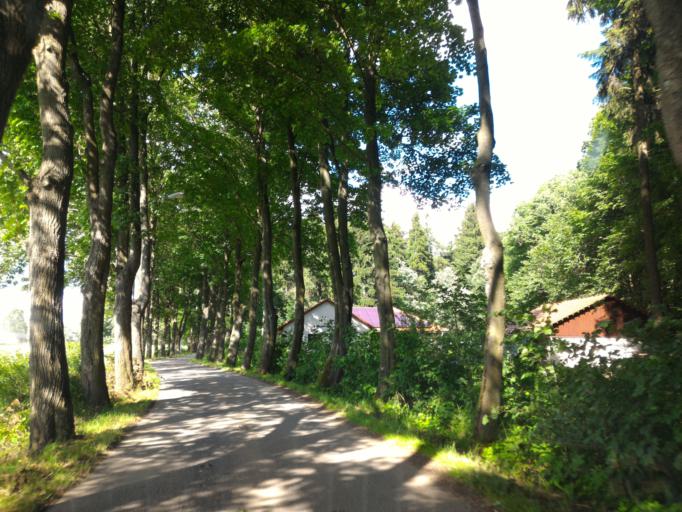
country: CZ
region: Vysocina
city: Velky Beranov
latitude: 49.4115
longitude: 15.6308
